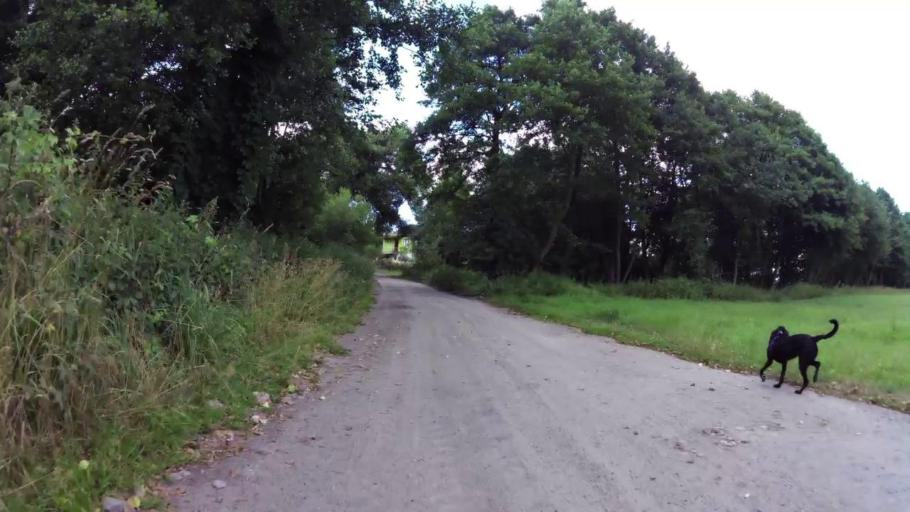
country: PL
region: West Pomeranian Voivodeship
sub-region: Powiat swidwinski
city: Swidwin
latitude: 53.6814
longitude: 15.7435
